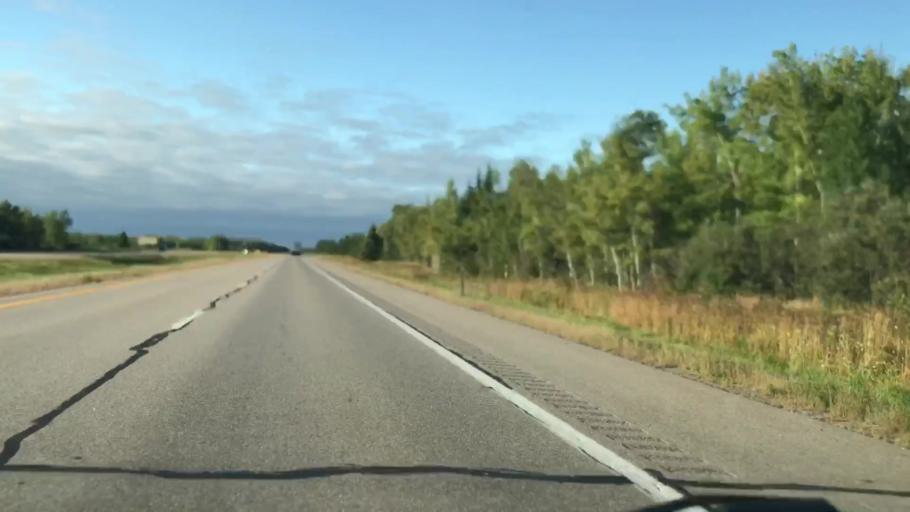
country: US
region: Michigan
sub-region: Chippewa County
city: Sault Ste. Marie
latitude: 46.4022
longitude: -84.4022
